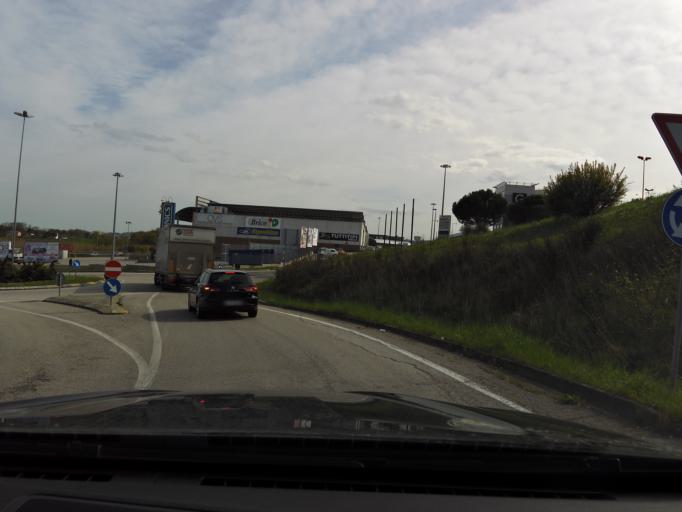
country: IT
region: The Marches
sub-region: Provincia di Ancona
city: Camerano
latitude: 43.5141
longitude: 13.5267
